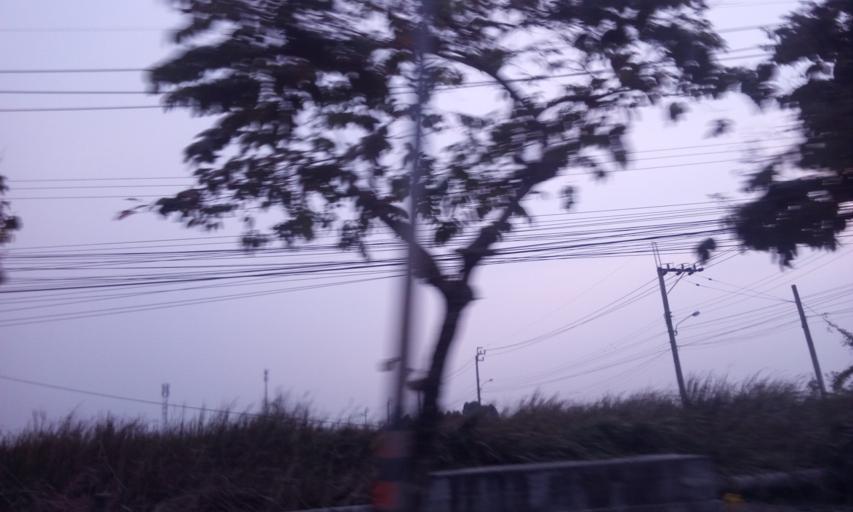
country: TH
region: Bangkok
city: Nong Chok
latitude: 13.8168
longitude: 100.9329
